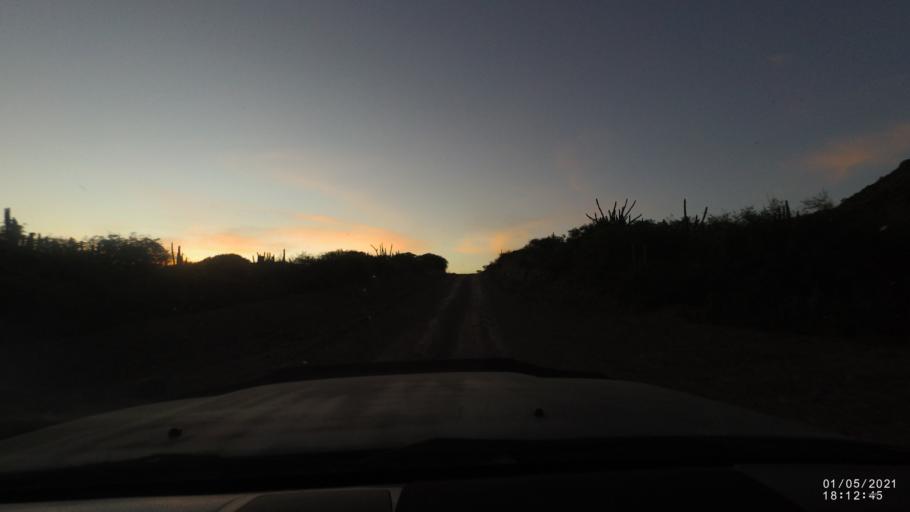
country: BO
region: Cochabamba
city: Capinota
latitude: -17.6771
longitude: -66.2031
